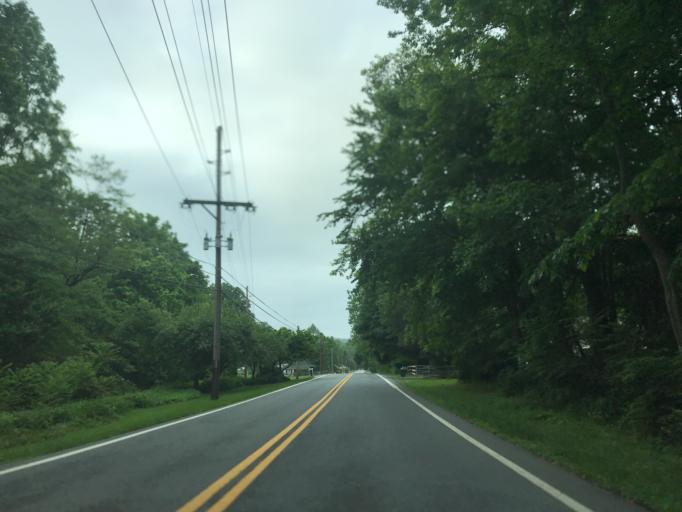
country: US
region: Maryland
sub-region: Frederick County
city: Thurmont
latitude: 39.5752
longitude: -77.4325
